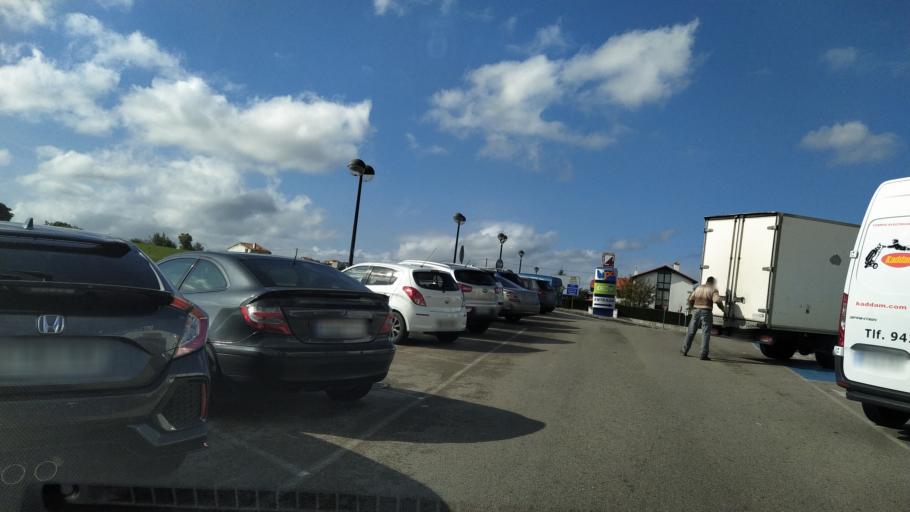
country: ES
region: Cantabria
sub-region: Provincia de Cantabria
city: Santa Cruz de Bezana
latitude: 43.4333
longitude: -3.9130
